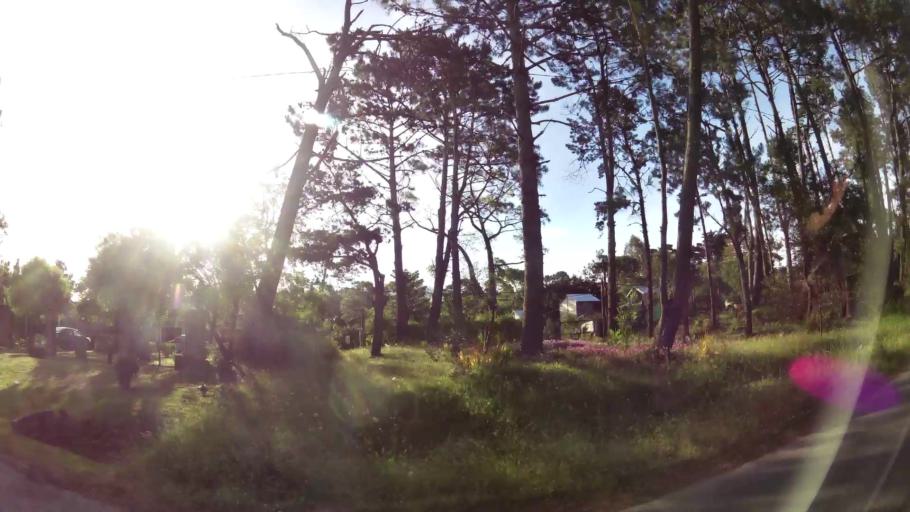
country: UY
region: Canelones
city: Empalme Olmos
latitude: -34.7821
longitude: -55.8527
